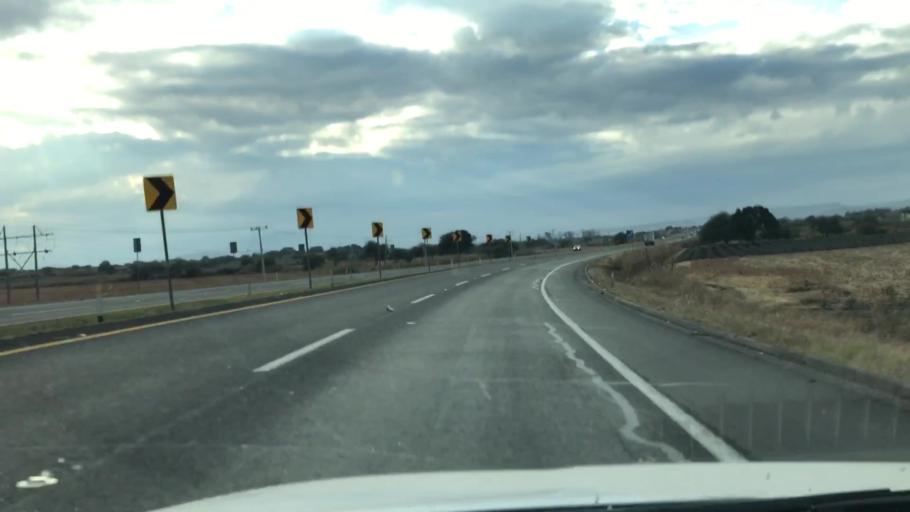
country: MX
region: Guanajuato
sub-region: Penjamo
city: Mezquite de Luna
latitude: 20.3778
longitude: -101.8500
